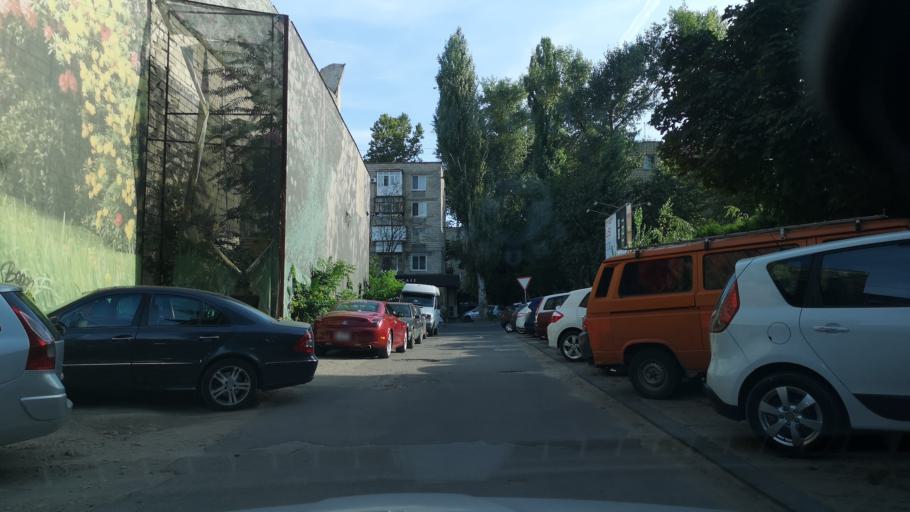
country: MD
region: Chisinau
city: Chisinau
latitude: 46.9987
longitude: 28.8583
